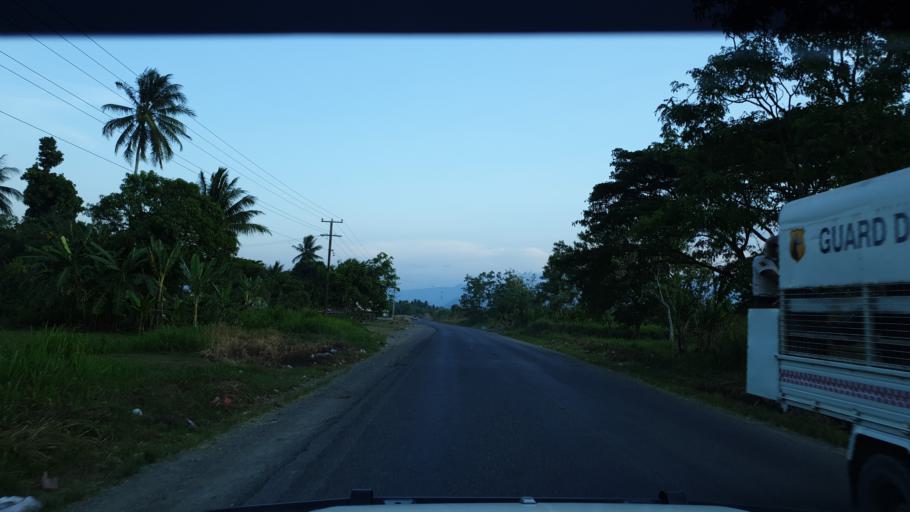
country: PG
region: Morobe
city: Lae
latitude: -6.5757
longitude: 146.7693
